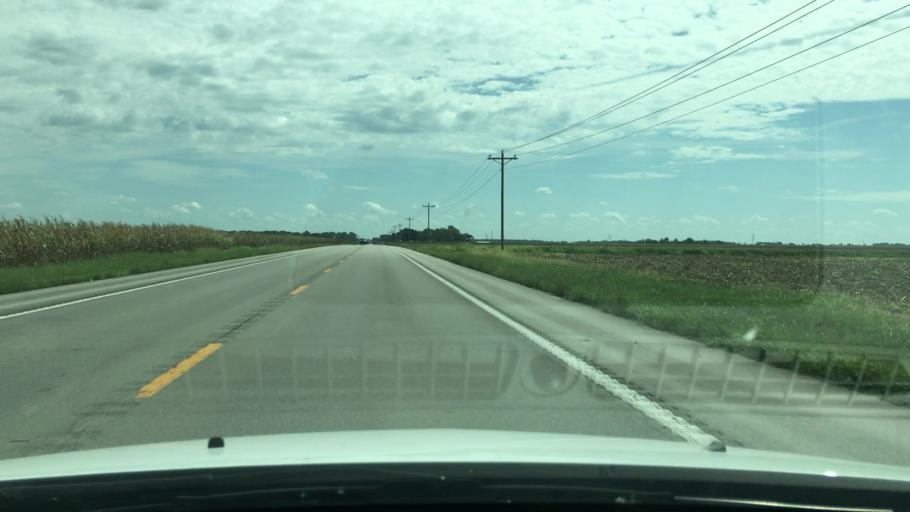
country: US
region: Missouri
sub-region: Audrain County
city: Mexico
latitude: 39.1639
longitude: -91.7726
